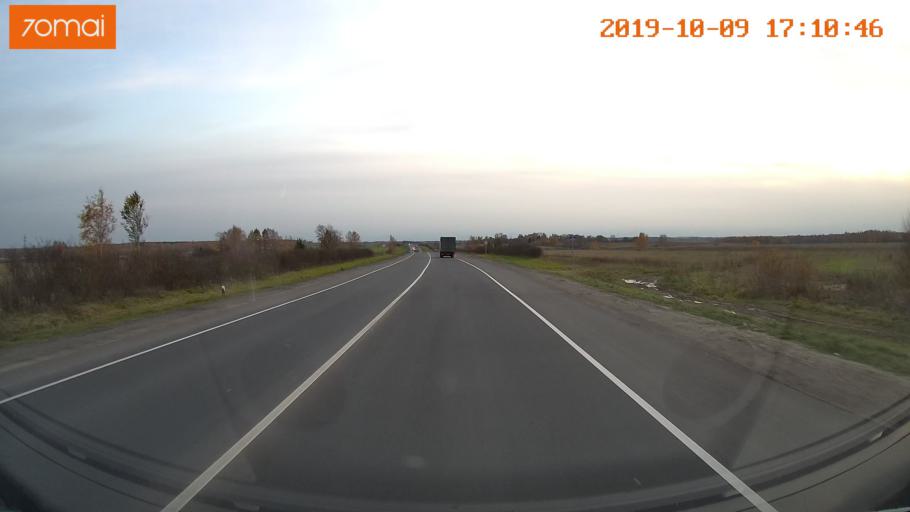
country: RU
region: Ivanovo
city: Privolzhsk
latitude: 57.3514
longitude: 41.2549
